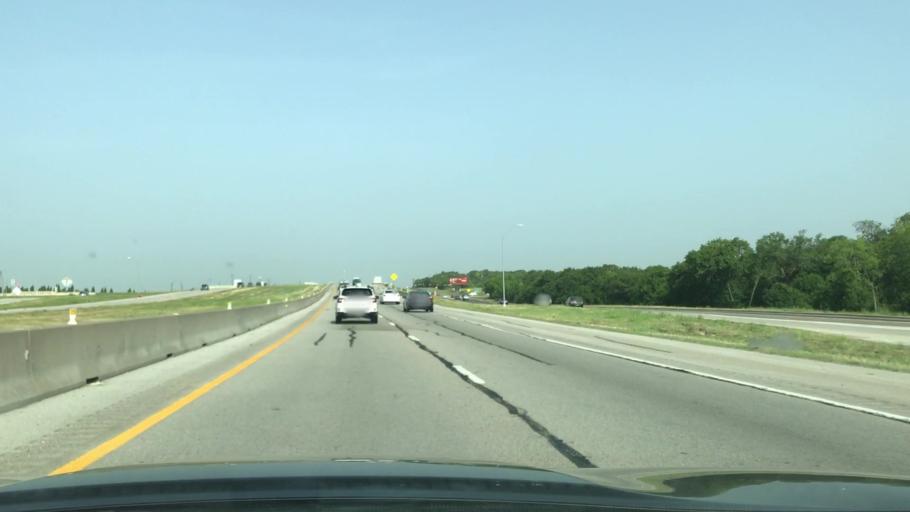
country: US
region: Texas
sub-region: Dallas County
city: Sunnyvale
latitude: 32.7844
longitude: -96.5583
